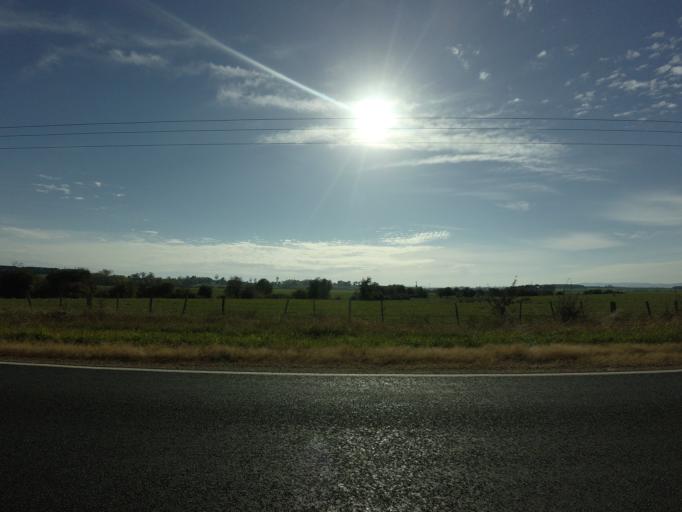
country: AU
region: Tasmania
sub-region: Meander Valley
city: Westbury
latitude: -41.5264
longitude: 146.9380
